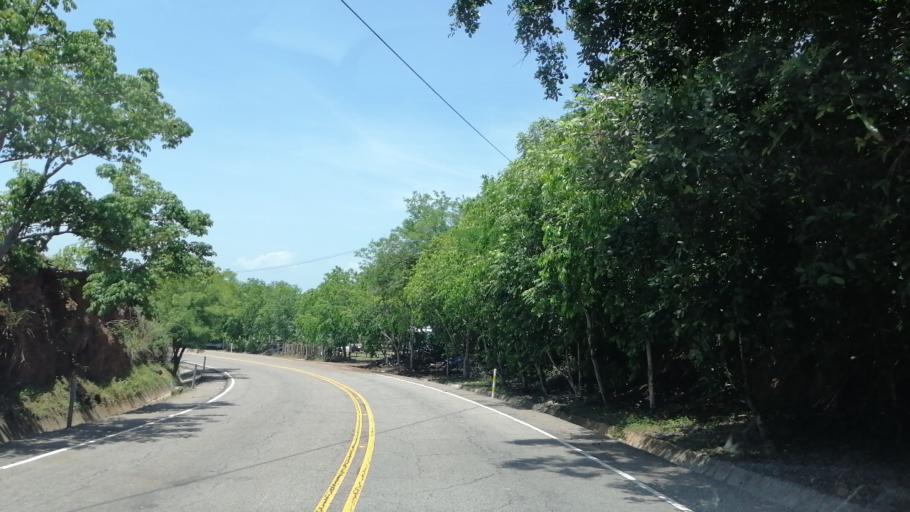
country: SV
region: Chalatenango
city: Nueva Concepcion
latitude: 14.1579
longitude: -89.3129
